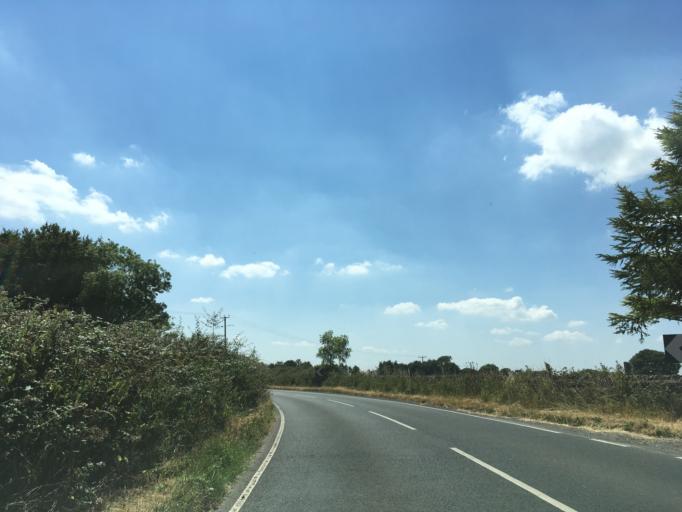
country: GB
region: England
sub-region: Gloucestershire
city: Chalford
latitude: 51.7402
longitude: -2.1511
